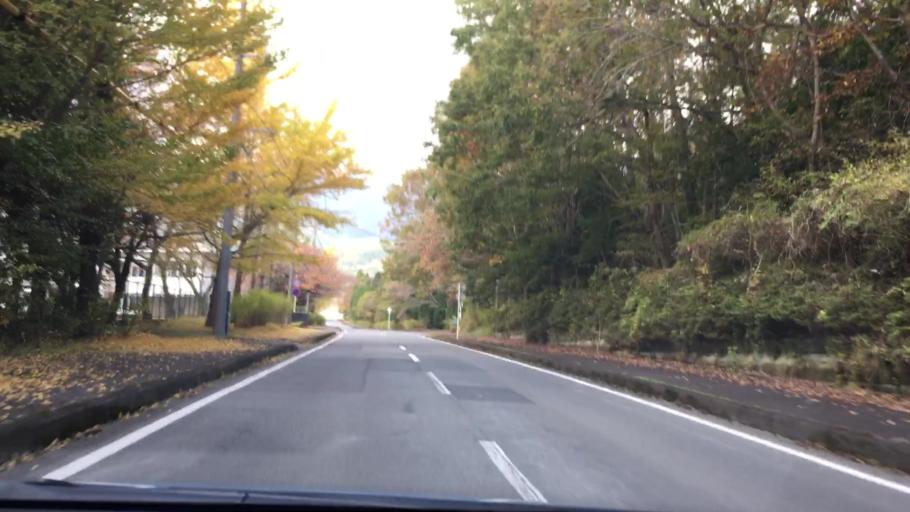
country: JP
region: Shizuoka
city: Gotemba
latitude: 35.3643
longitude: 138.9410
